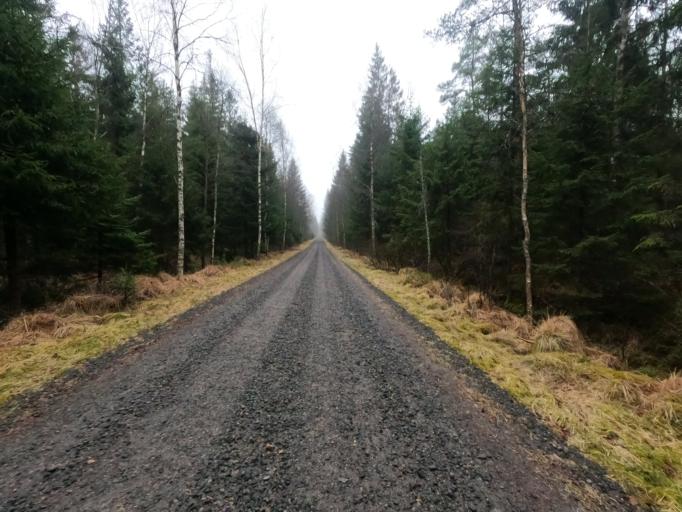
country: SE
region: Halland
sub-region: Hylte Kommun
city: Hyltebruk
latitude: 56.8152
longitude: 13.3151
